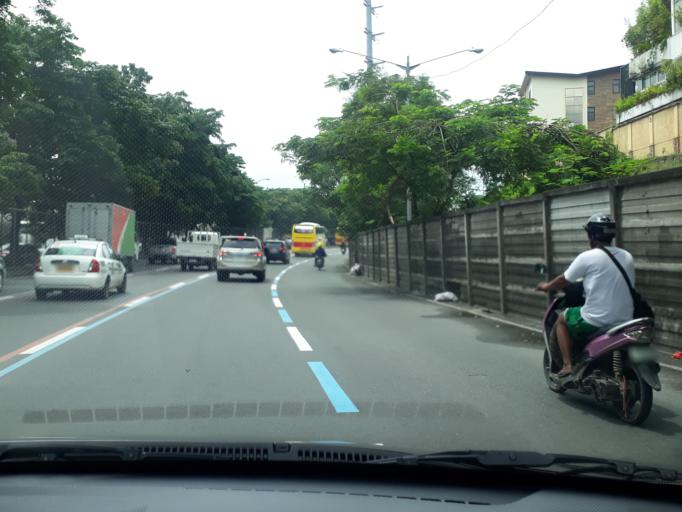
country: PH
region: Calabarzon
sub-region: Province of Rizal
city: Pateros
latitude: 14.5401
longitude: 121.0562
